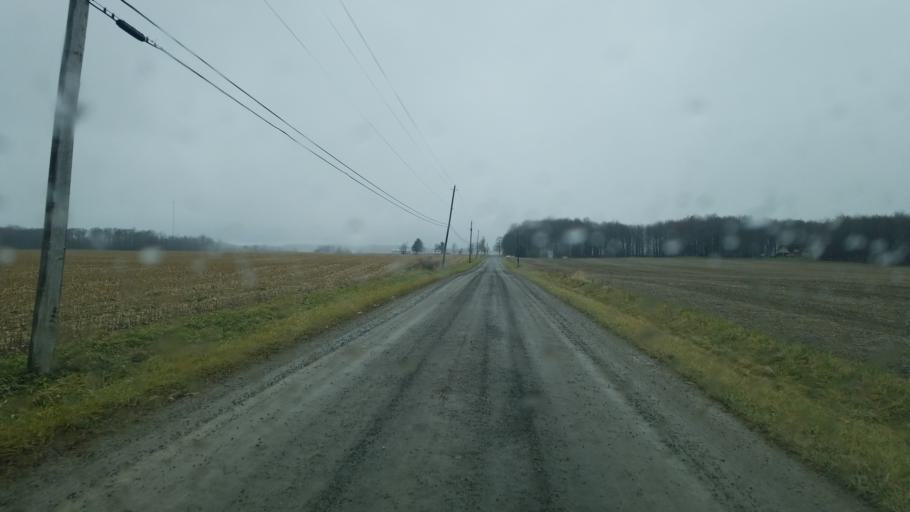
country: US
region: Ohio
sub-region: Ashtabula County
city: Roaming Shores
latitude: 41.5926
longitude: -80.7052
